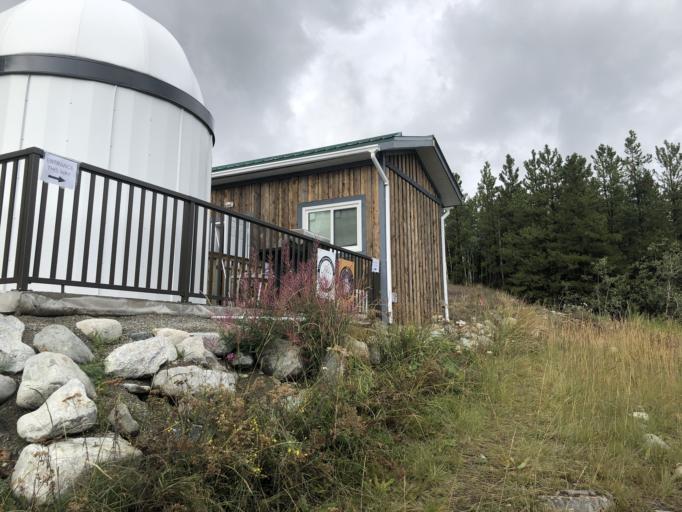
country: CA
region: Yukon
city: Whitehorse
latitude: 60.8800
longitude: -135.3619
